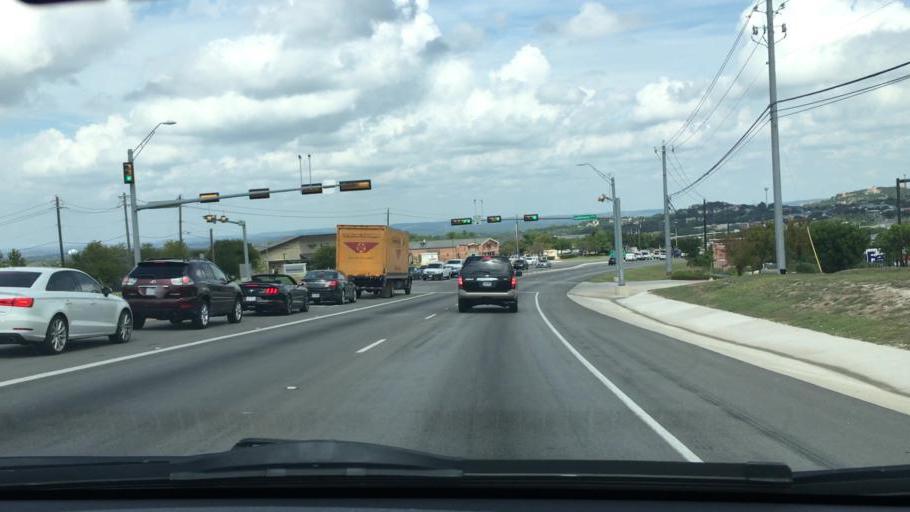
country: US
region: Texas
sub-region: Travis County
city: The Hills
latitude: 30.3382
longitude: -97.9698
